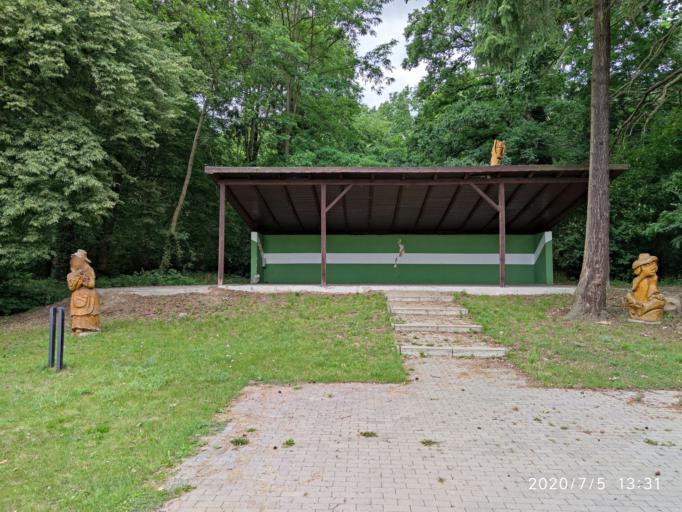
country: PL
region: Lubusz
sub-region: Powiat zielonogorski
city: Swidnica
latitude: 51.8932
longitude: 15.3951
